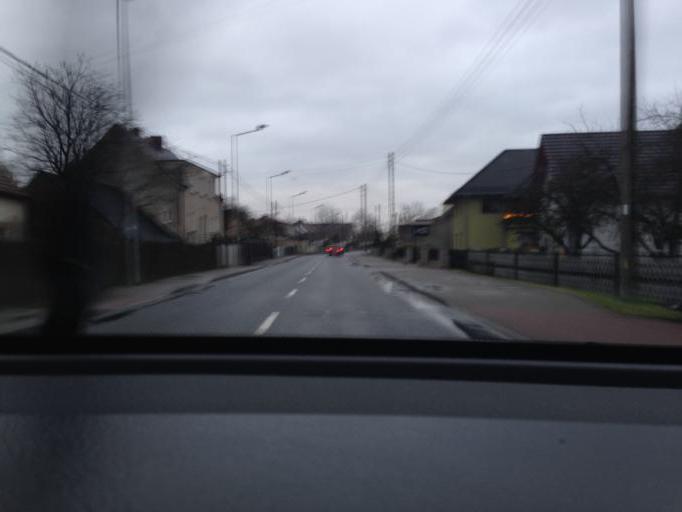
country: PL
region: Opole Voivodeship
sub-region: Powiat opolski
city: Opole
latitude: 50.6898
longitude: 17.9507
